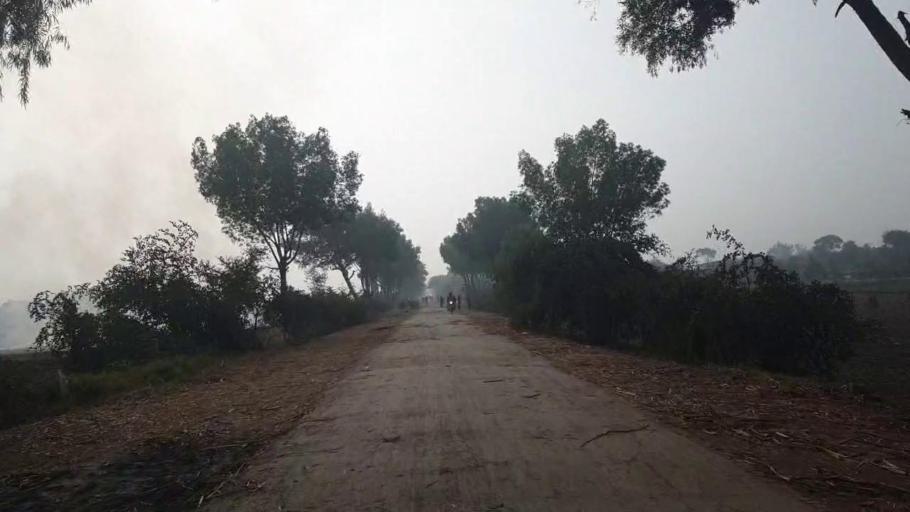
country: PK
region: Sindh
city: Tando Adam
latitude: 25.7706
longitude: 68.6073
